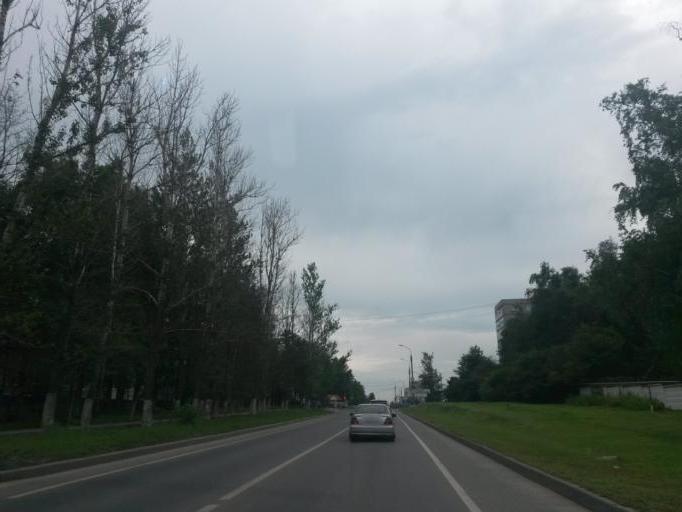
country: RU
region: Moskovskaya
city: Vostryakovo
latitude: 55.4181
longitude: 37.8386
